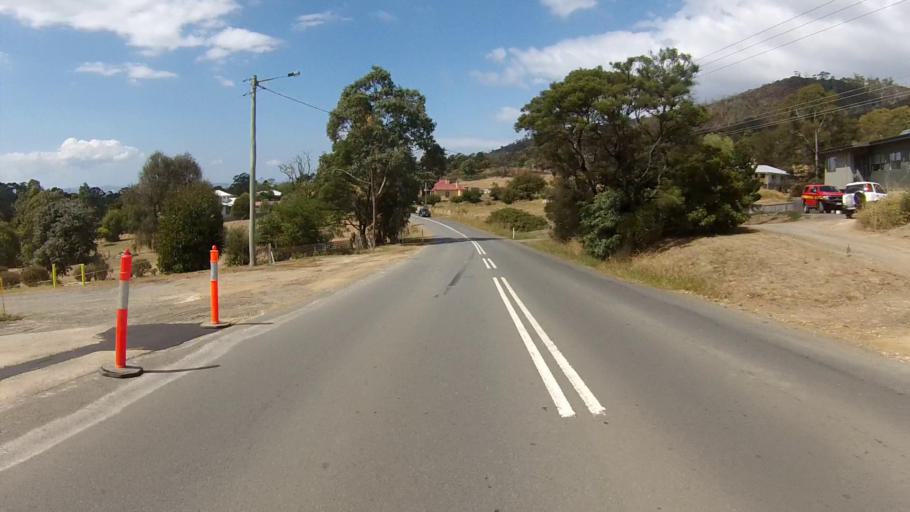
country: AU
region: Tasmania
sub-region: Clarence
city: Cambridge
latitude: -42.8385
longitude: 147.4300
